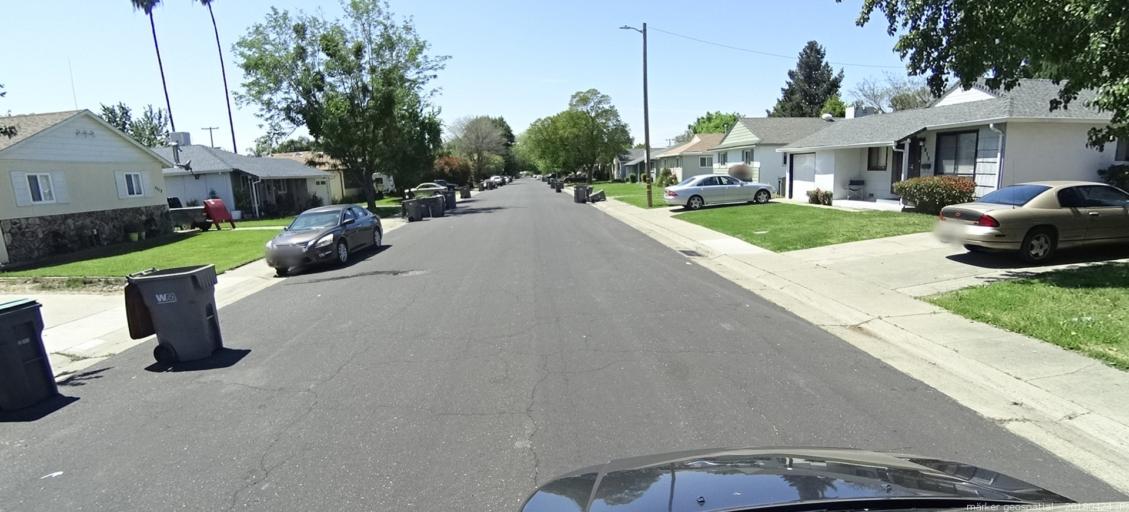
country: US
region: California
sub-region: Yolo County
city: West Sacramento
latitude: 38.5831
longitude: -121.5286
